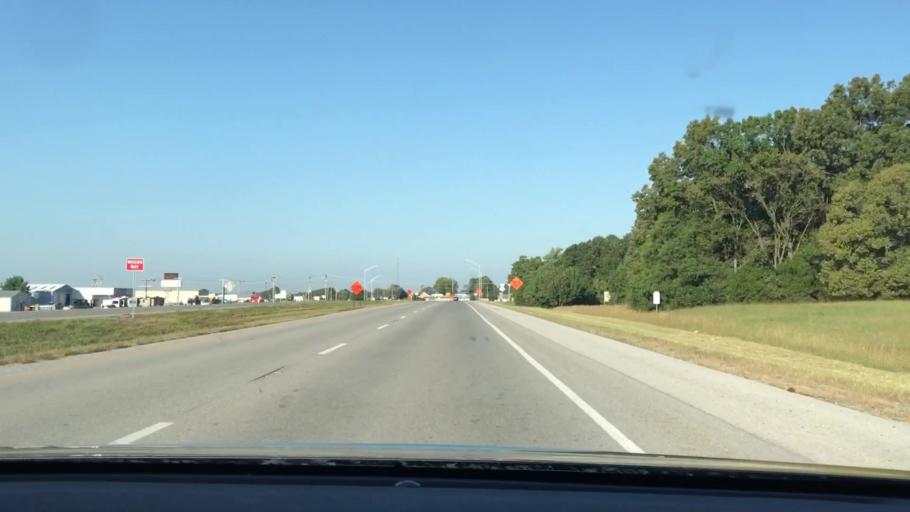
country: US
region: Kentucky
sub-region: Trigg County
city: Cadiz
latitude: 36.8678
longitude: -87.7886
